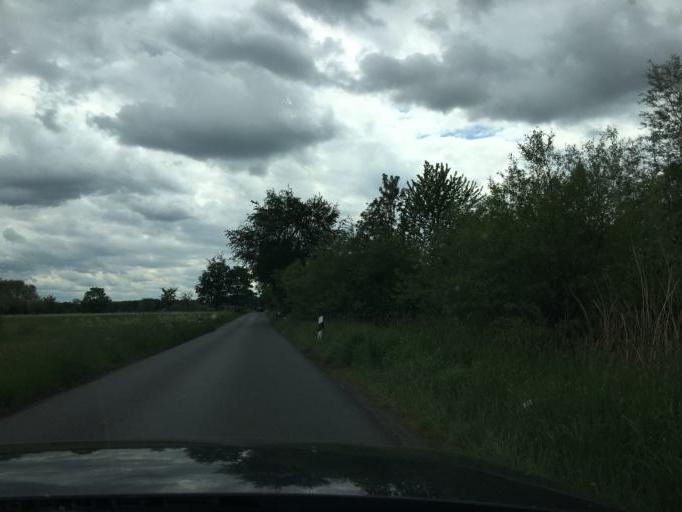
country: DE
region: North Rhine-Westphalia
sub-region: Regierungsbezirk Munster
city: Muenster
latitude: 52.0214
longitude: 7.6468
